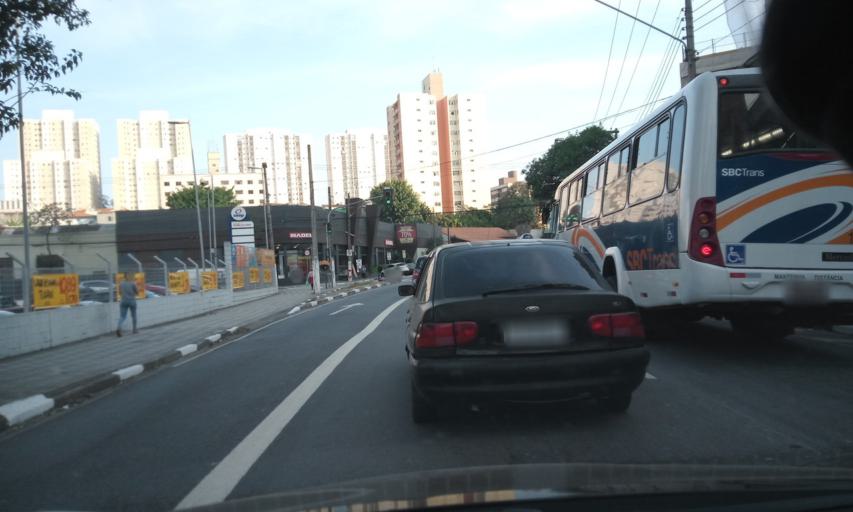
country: BR
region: Sao Paulo
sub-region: Sao Bernardo Do Campo
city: Sao Bernardo do Campo
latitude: -23.7150
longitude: -46.5540
